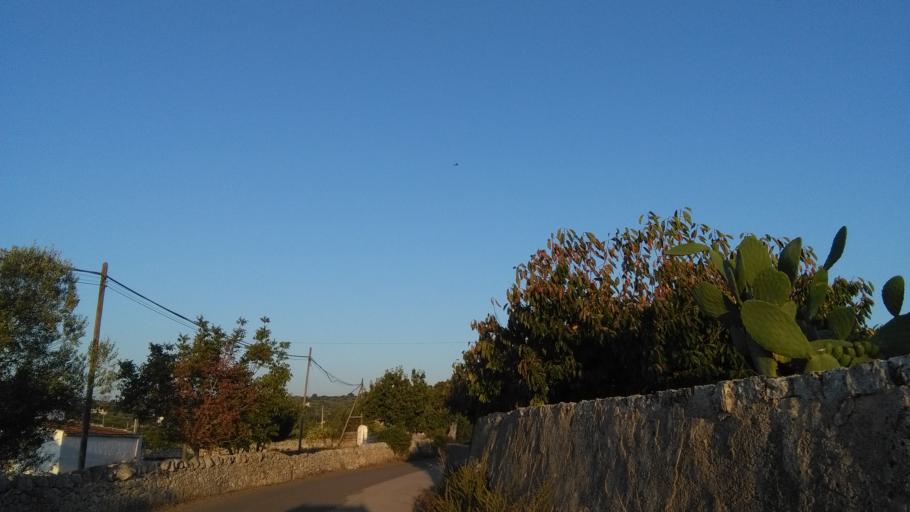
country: IT
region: Apulia
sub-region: Provincia di Bari
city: Putignano
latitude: 40.8280
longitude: 17.1053
